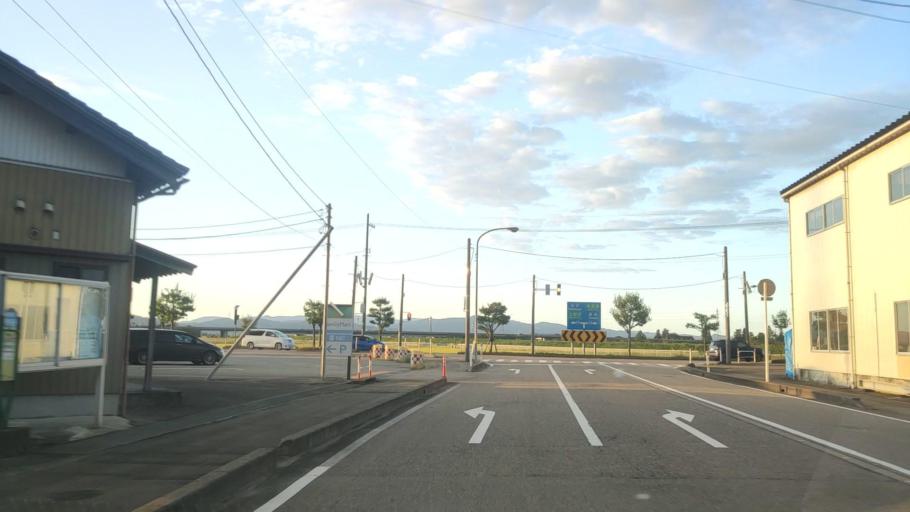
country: JP
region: Toyama
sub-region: Oyabe Shi
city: Oyabe
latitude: 36.6261
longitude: 136.8883
